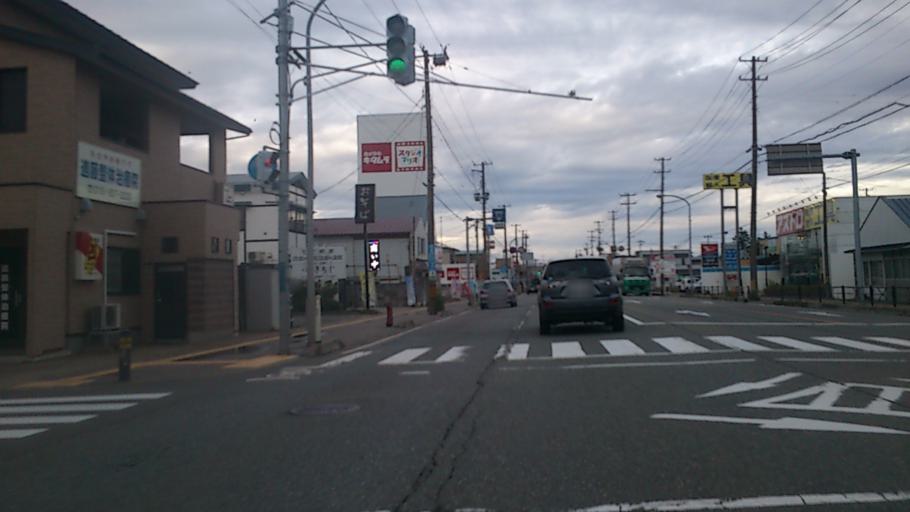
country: JP
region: Akita
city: Akita Shi
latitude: 39.7469
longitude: 140.0823
